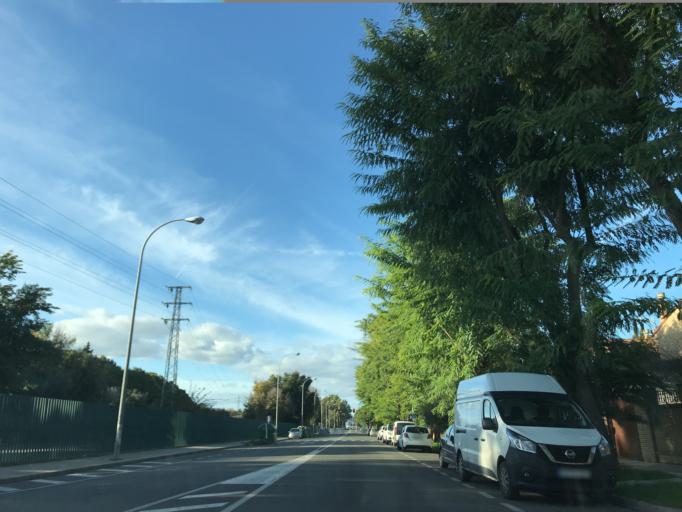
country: ES
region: Andalusia
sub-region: Provincia de Sevilla
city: Sevilla
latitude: 37.3951
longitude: -5.9285
